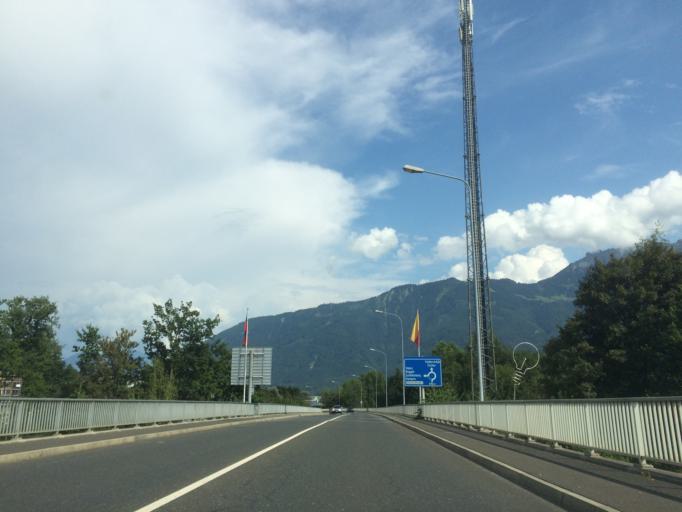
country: CH
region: Saint Gallen
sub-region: Wahlkreis Werdenberg
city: Haag (Rheintal)
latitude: 47.2101
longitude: 9.4992
